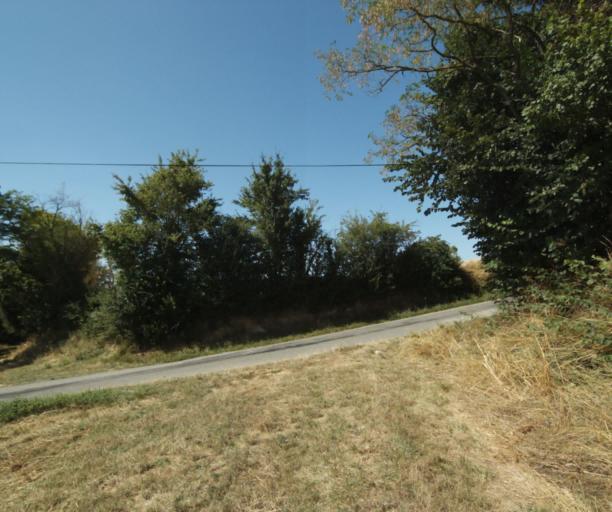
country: FR
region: Midi-Pyrenees
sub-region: Departement de la Haute-Garonne
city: Saint-Felix-Lauragais
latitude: 43.4913
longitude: 1.8924
